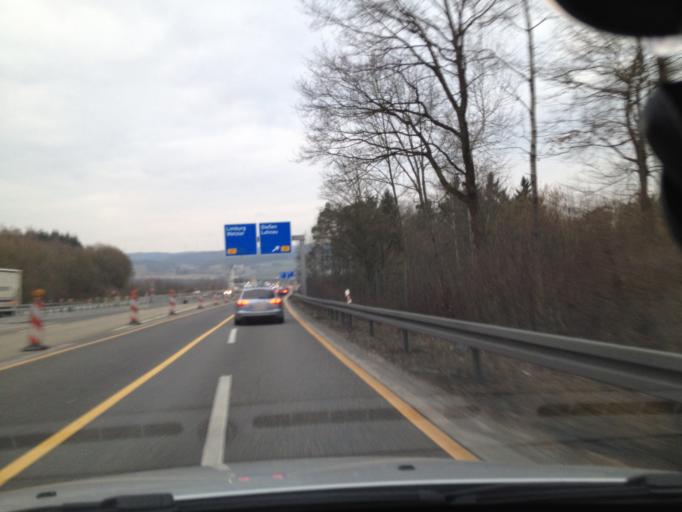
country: DE
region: Hesse
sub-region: Regierungsbezirk Giessen
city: Wetzlar
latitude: 50.5673
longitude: 8.5486
